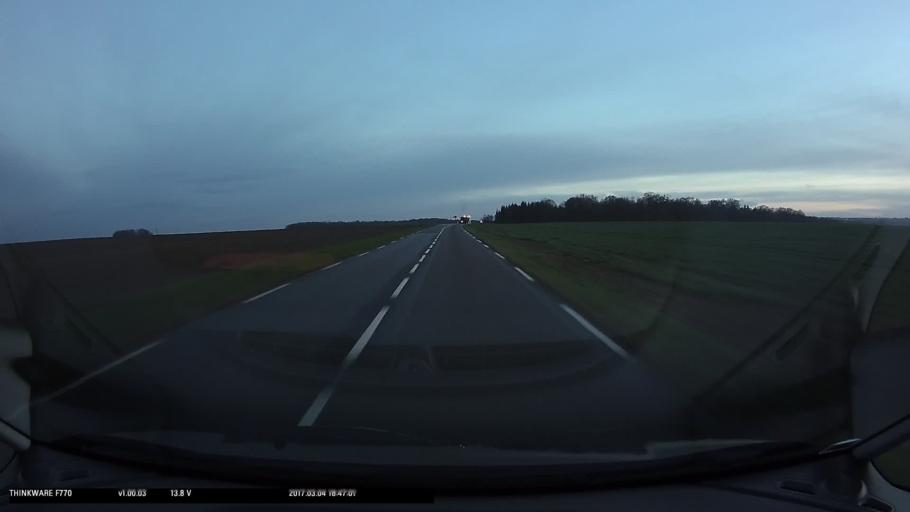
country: FR
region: Ile-de-France
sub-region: Departement du Val-d'Oise
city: Us
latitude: 49.1192
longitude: 1.9818
